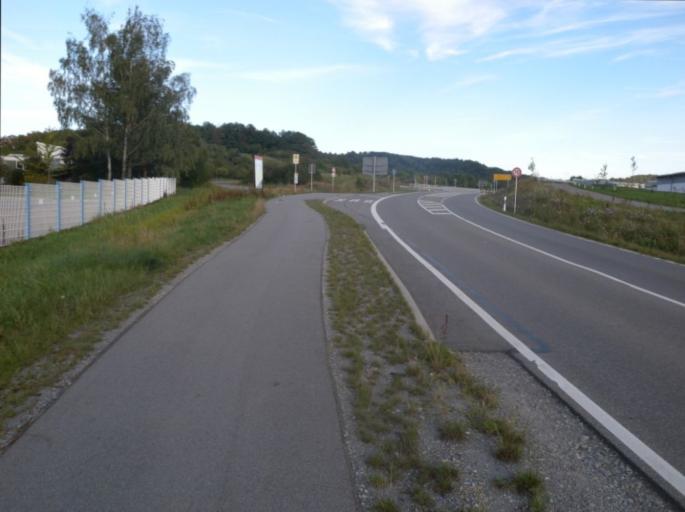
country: DE
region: Baden-Wuerttemberg
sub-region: Regierungsbezirk Stuttgart
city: Leutenbach
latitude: 48.9016
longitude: 9.4174
